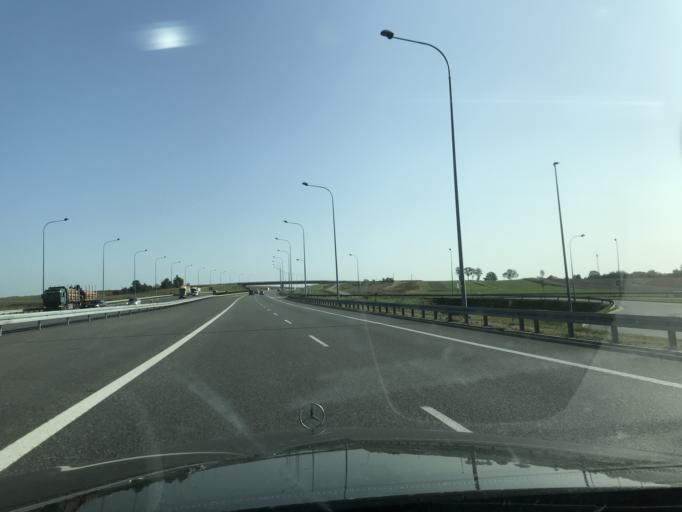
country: PL
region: Subcarpathian Voivodeship
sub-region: Powiat debicki
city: Czarna
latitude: 50.0979
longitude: 21.2243
